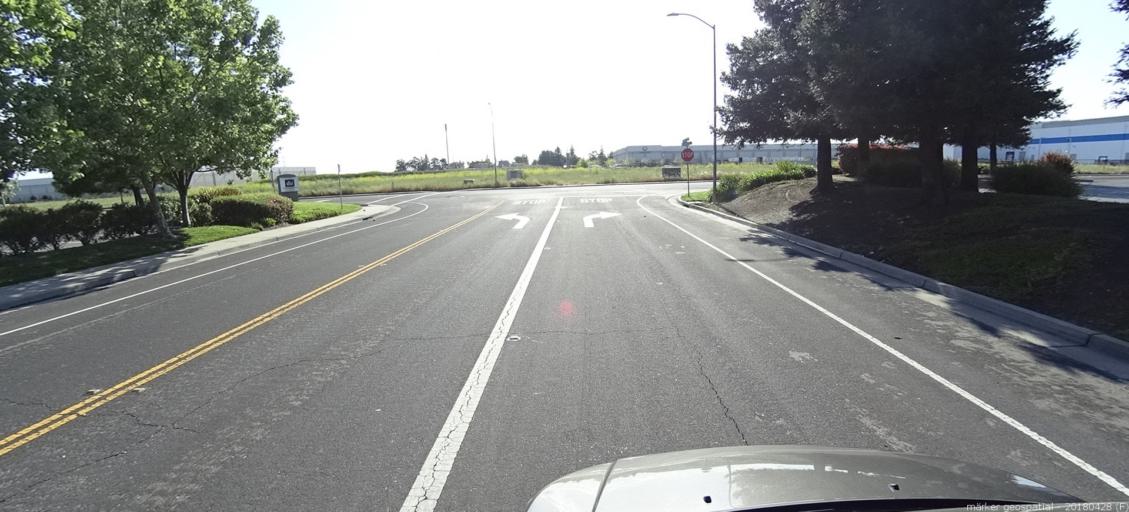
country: US
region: California
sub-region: Yolo County
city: West Sacramento
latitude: 38.5510
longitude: -121.5635
